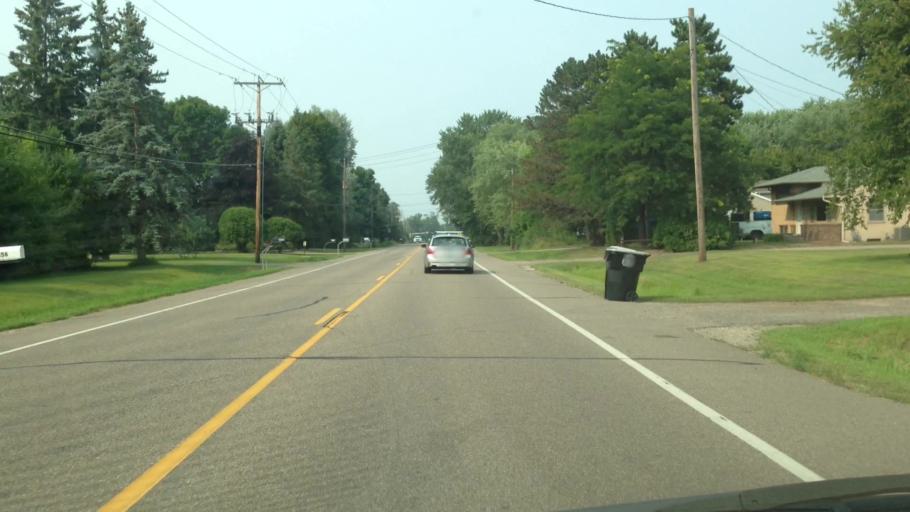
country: US
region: Minnesota
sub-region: Anoka County
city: Circle Pines
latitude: 45.1369
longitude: -93.1272
